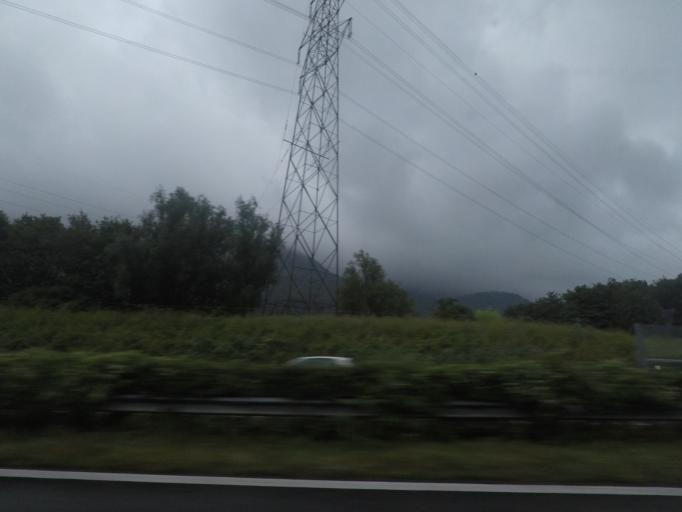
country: CH
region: Valais
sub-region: Martigny District
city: Evionnaz
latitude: 46.1806
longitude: 7.0263
